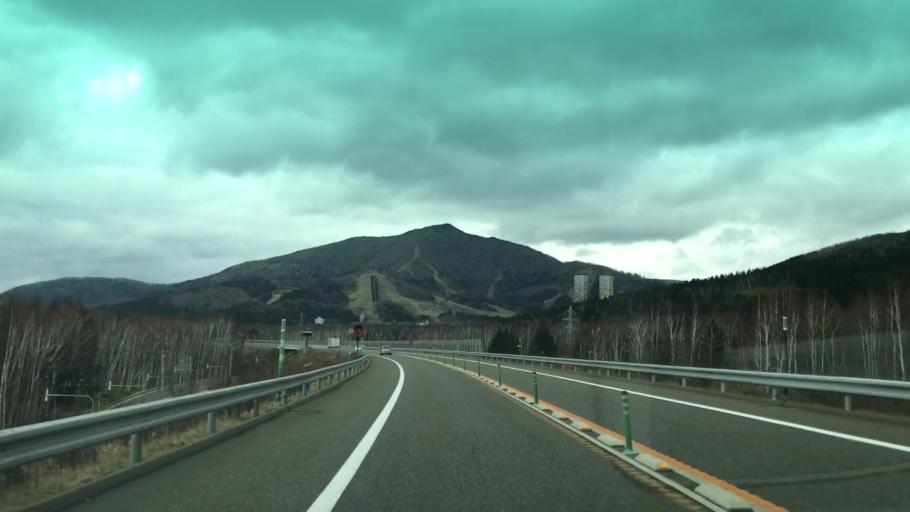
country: JP
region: Hokkaido
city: Shimo-furano
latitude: 43.0515
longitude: 142.6474
